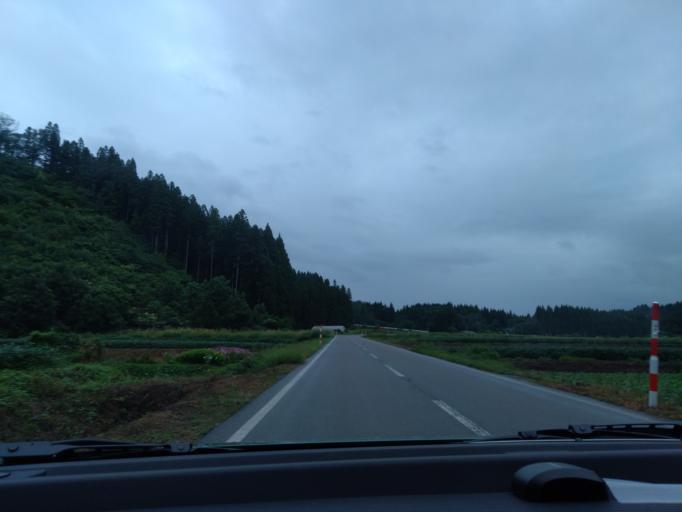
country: JP
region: Akita
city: Yokotemachi
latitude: 39.3840
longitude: 140.5834
